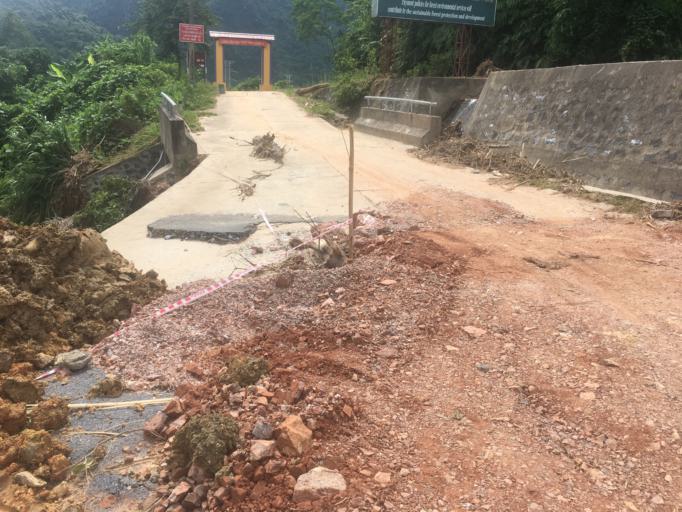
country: VN
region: Ha Giang
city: Thanh Pho Ha Giang
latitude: 22.8559
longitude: 105.0241
